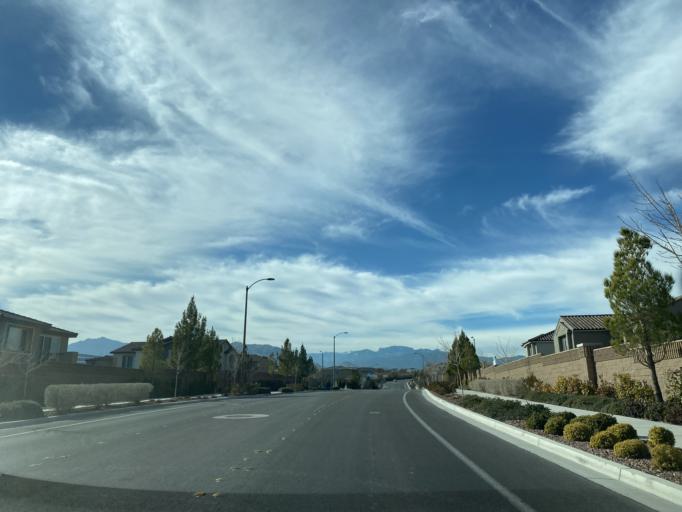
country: US
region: Nevada
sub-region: Clark County
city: Summerlin South
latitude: 36.3106
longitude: -115.3136
